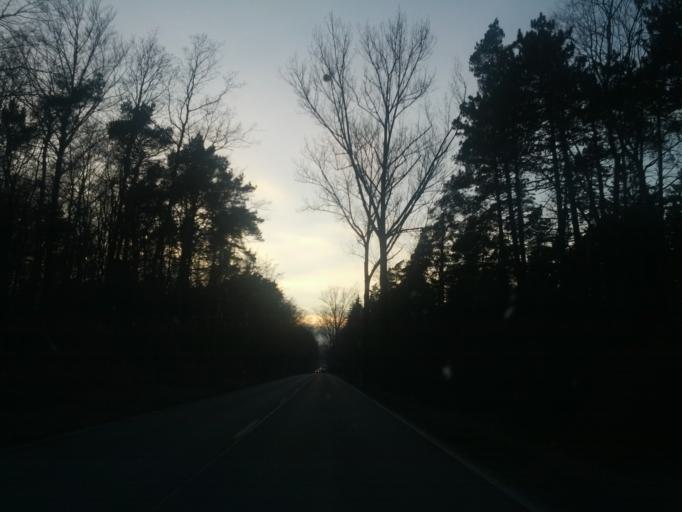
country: DE
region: Thuringia
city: Oberdorla
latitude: 51.2077
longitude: 10.3838
